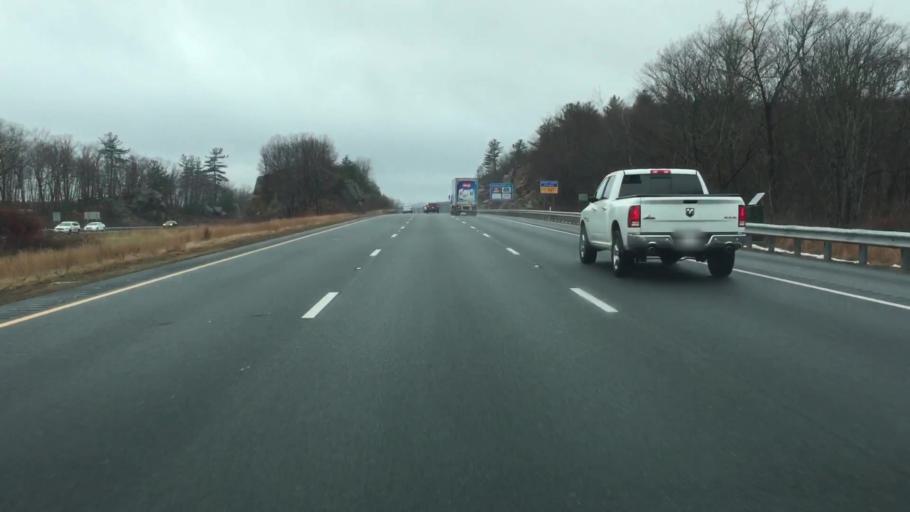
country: US
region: Massachusetts
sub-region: Worcester County
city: Milford
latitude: 42.1624
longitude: -71.4978
